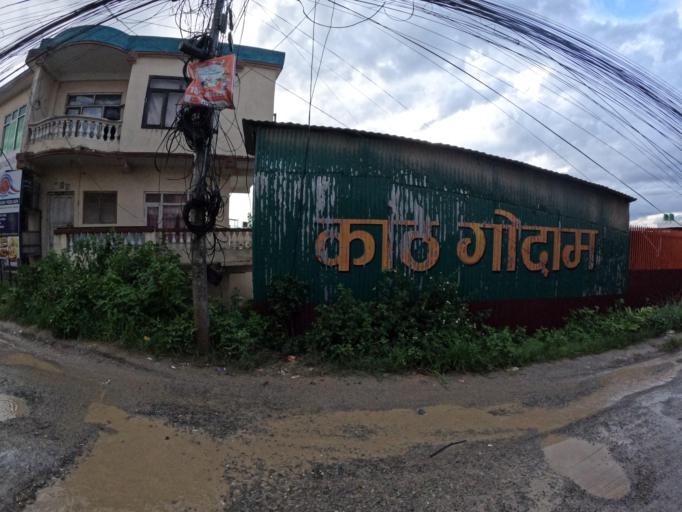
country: NP
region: Central Region
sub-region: Bagmati Zone
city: Kathmandu
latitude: 27.7594
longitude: 85.3286
